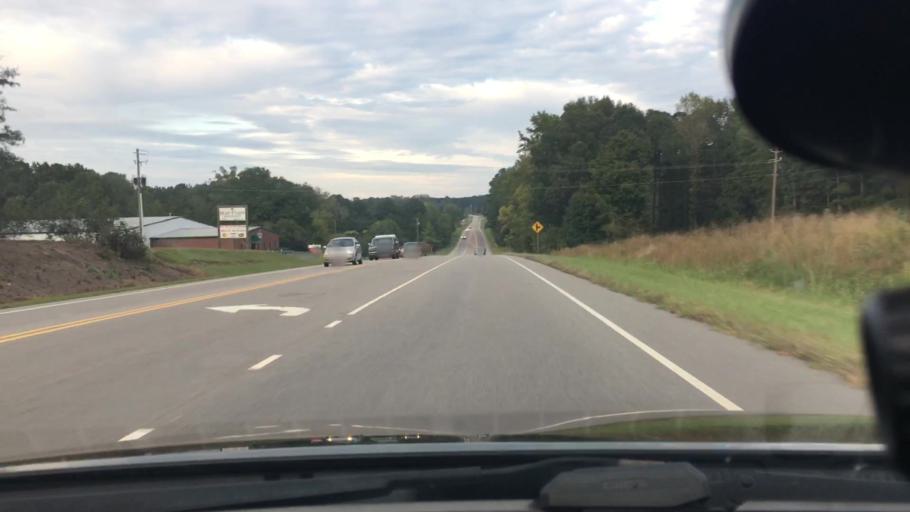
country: US
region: North Carolina
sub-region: Lee County
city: Sanford
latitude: 35.3963
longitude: -79.2417
